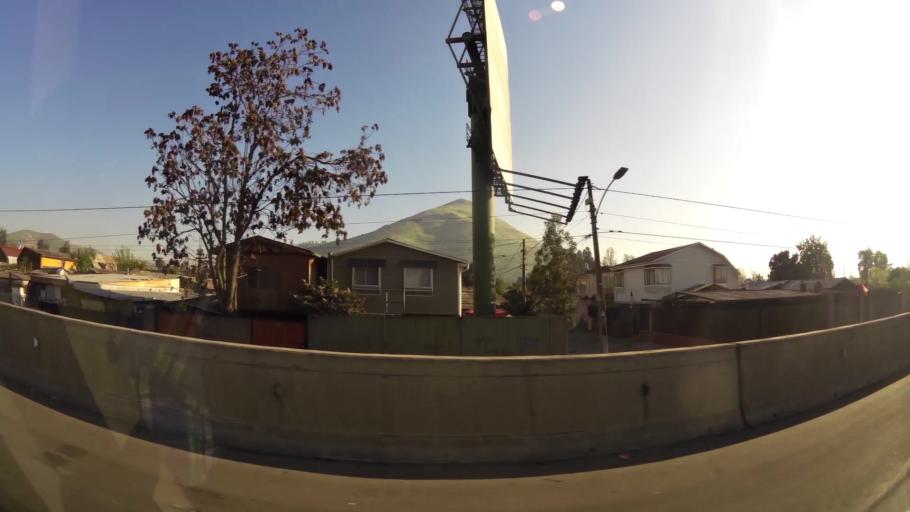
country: CL
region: Santiago Metropolitan
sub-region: Provincia de Santiago
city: Lo Prado
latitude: -33.4072
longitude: -70.7117
